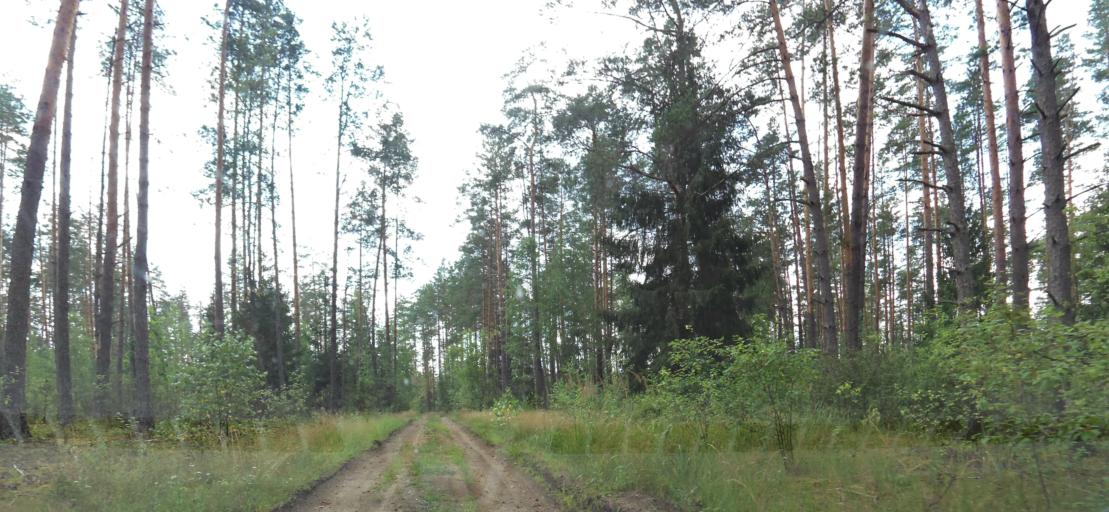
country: LT
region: Alytaus apskritis
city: Varena
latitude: 54.2417
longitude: 24.6540
